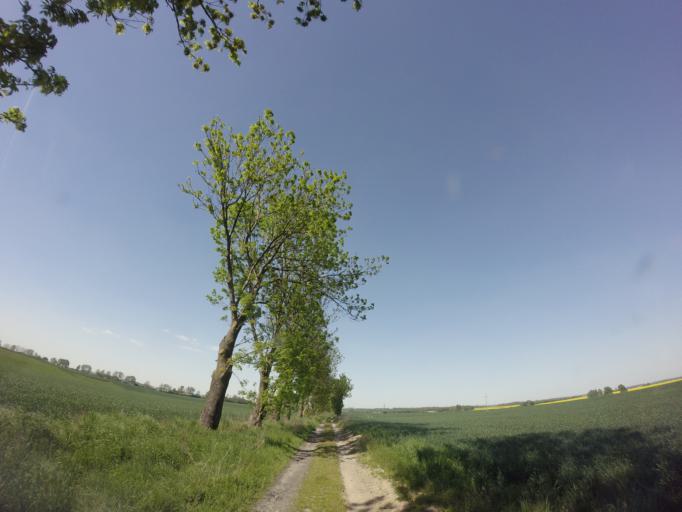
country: PL
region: West Pomeranian Voivodeship
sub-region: Powiat choszczenski
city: Pelczyce
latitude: 53.0574
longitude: 15.3827
